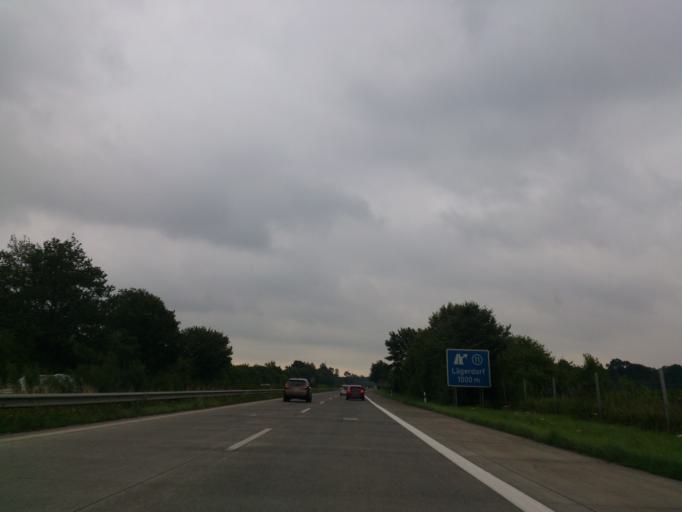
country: DE
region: Schleswig-Holstein
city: Neuenbrook
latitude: 53.8804
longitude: 9.5492
